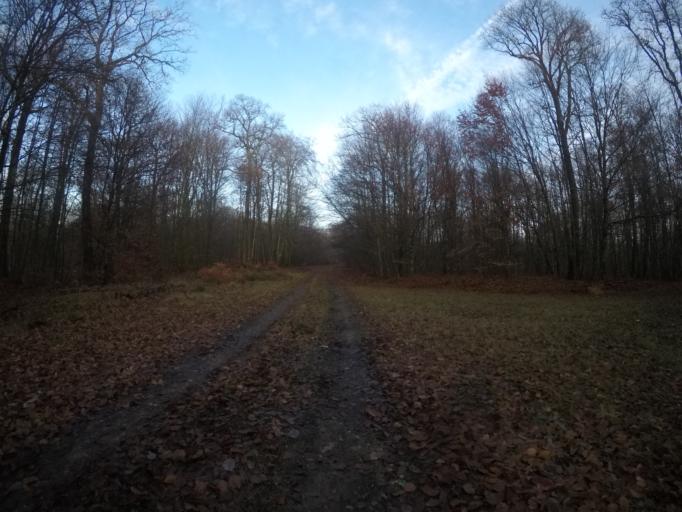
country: BE
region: Wallonia
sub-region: Province du Luxembourg
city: Habay-la-Vieille
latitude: 49.7519
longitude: 5.6714
